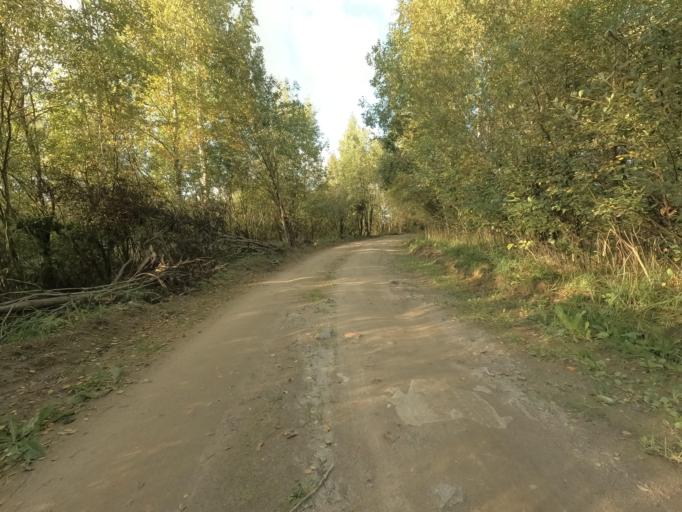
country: RU
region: Leningrad
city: Imeni Sverdlova
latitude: 59.8572
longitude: 30.7322
